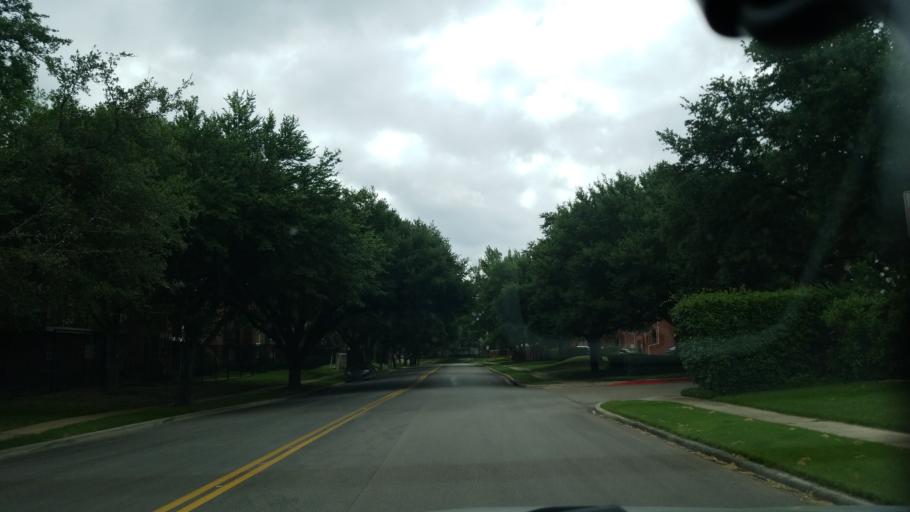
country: US
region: Texas
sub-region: Dallas County
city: Farmers Branch
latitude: 32.9358
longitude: -96.9475
